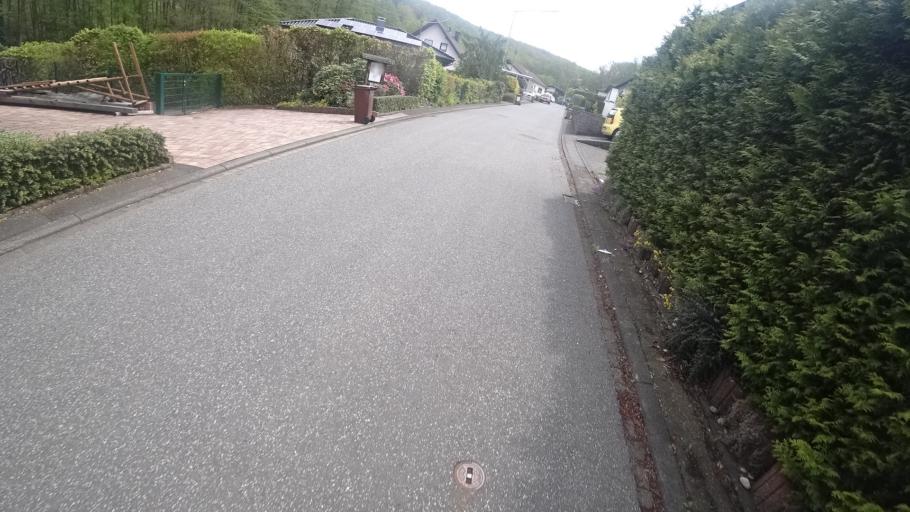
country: DE
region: Rheinland-Pfalz
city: Scheuerfeld
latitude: 50.7837
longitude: 7.8490
